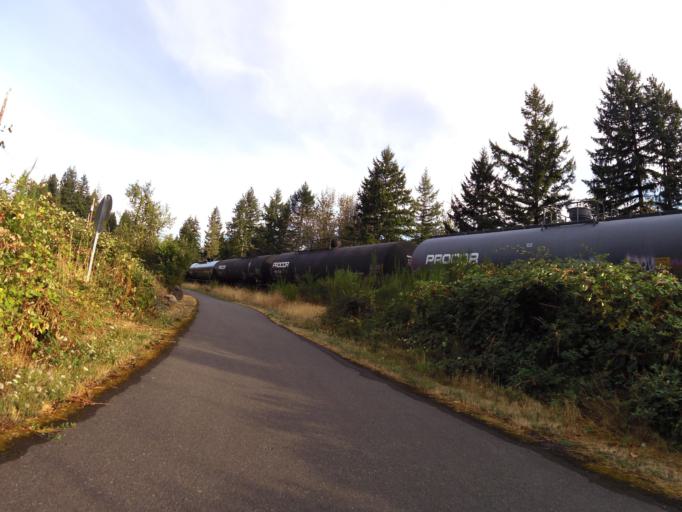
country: US
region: Washington
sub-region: Thurston County
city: Rainier
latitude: 46.9063
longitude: -122.7730
